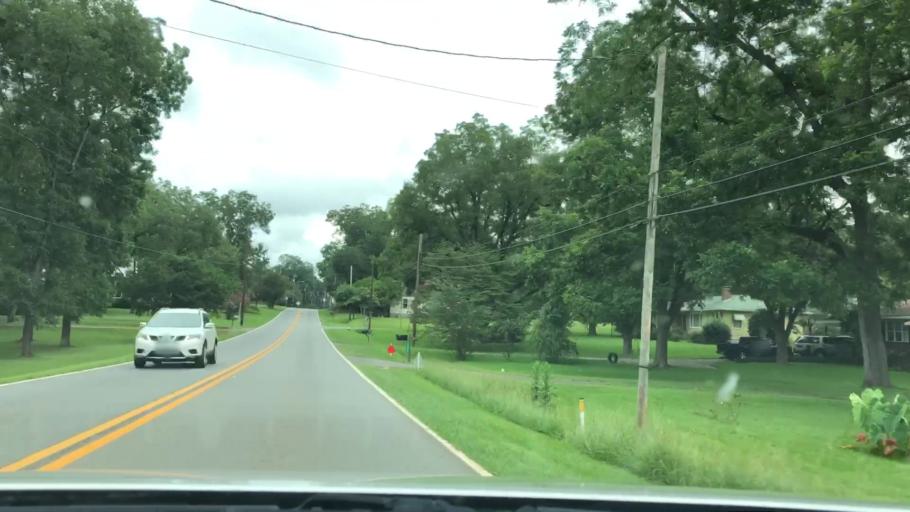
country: US
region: Georgia
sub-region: Pike County
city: Zebulon
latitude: 33.1020
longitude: -84.3499
